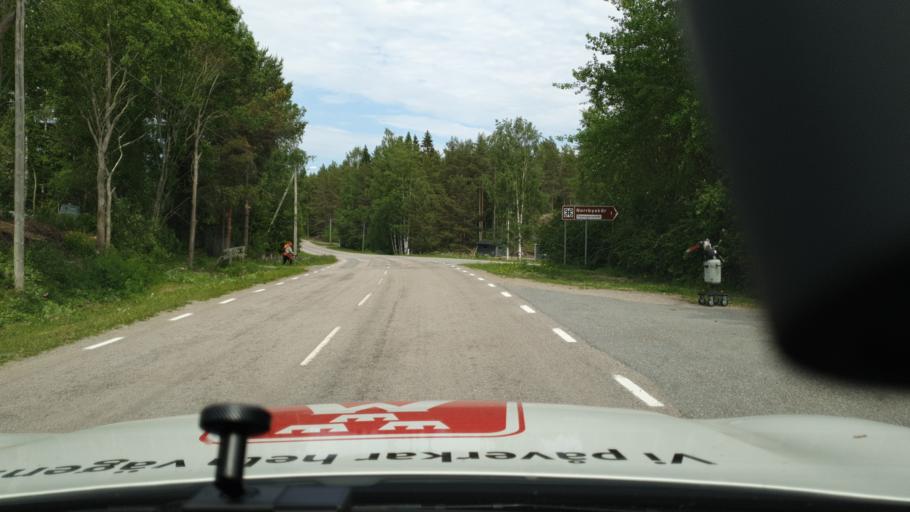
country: SE
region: Vaesterbotten
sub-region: Umea Kommun
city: Hoernefors
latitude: 63.5684
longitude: 19.8227
